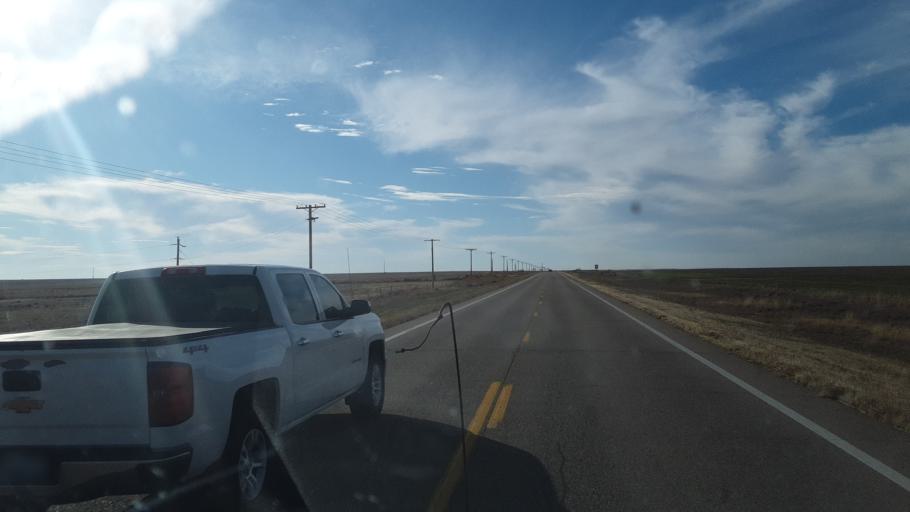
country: US
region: Kansas
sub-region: Finney County
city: Garden City
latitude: 38.0601
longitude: -100.6106
